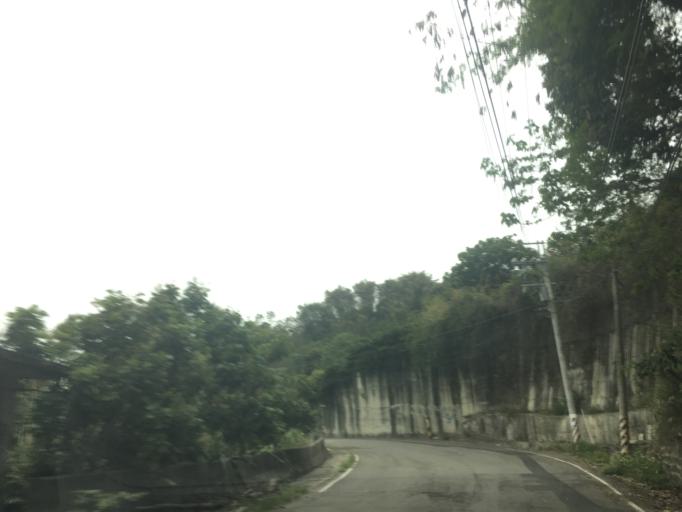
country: TW
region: Taiwan
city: Zhongxing New Village
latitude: 24.0320
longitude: 120.7230
